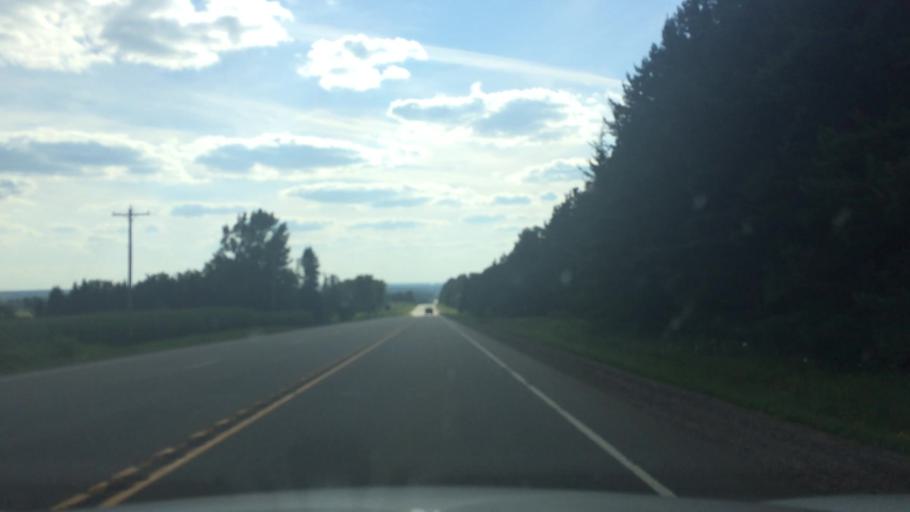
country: US
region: Wisconsin
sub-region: Lincoln County
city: Merrill
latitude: 45.1780
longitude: -89.6150
